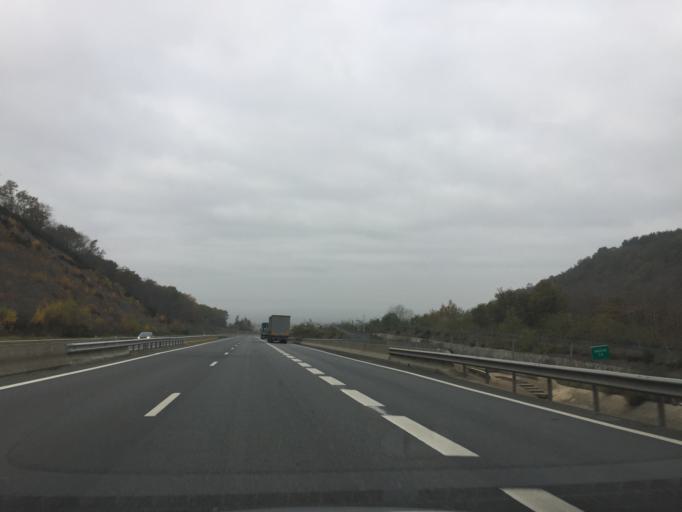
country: FR
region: Auvergne
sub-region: Departement de l'Allier
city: Desertines
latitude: 46.3675
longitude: 2.6382
